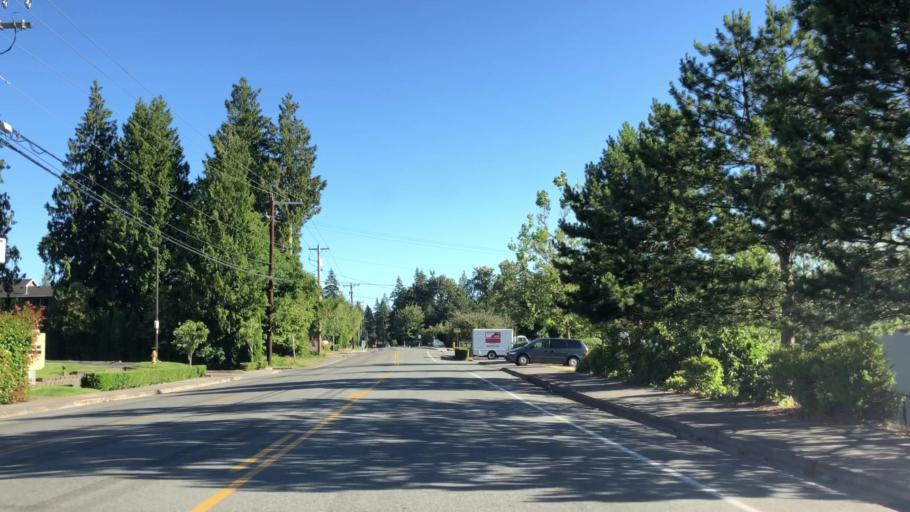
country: US
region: Washington
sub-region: Snohomish County
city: Martha Lake
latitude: 47.8483
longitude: -122.2516
